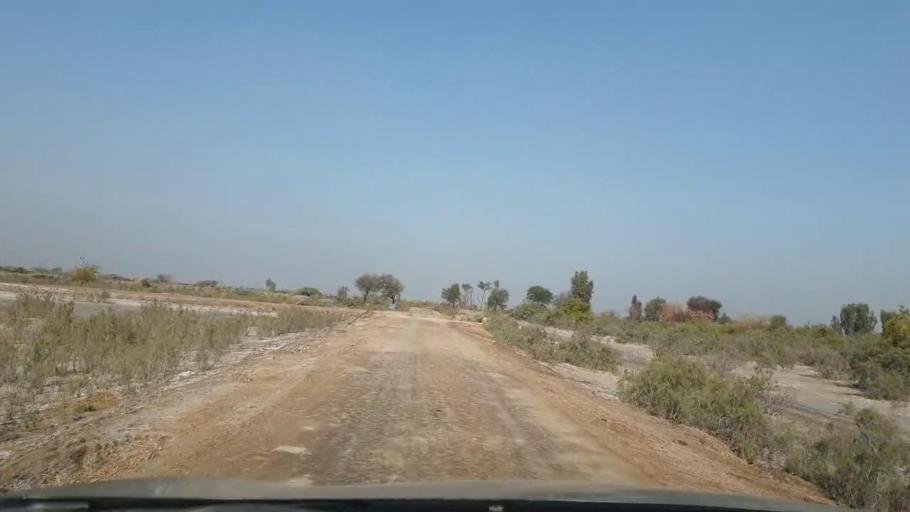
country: PK
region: Sindh
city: Berani
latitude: 25.6852
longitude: 68.8896
